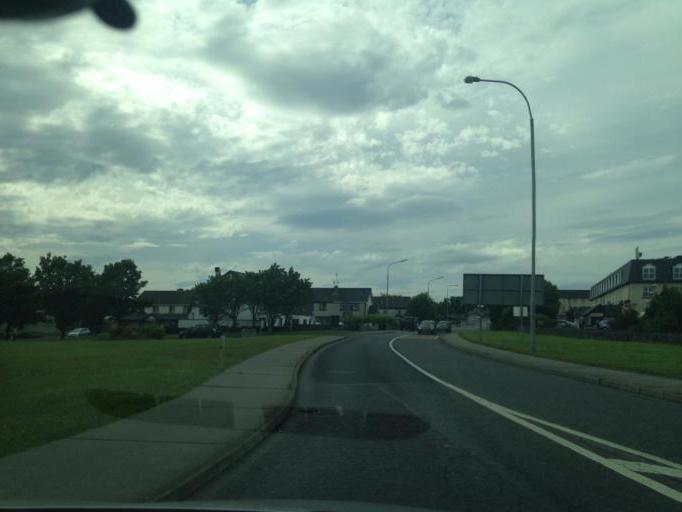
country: IE
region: Connaught
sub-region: County Galway
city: Gaillimh
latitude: 53.2870
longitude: -9.0457
